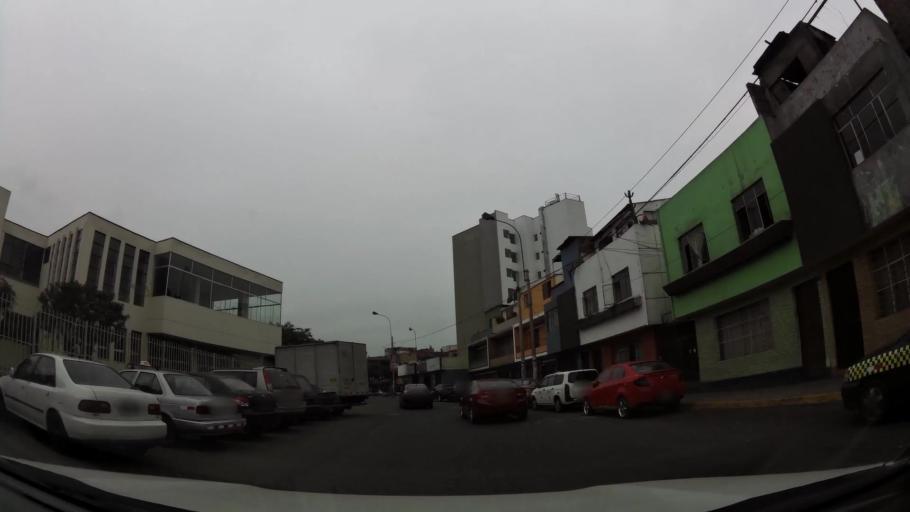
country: PE
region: Lima
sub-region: Lima
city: San Luis
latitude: -12.0781
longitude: -77.0231
